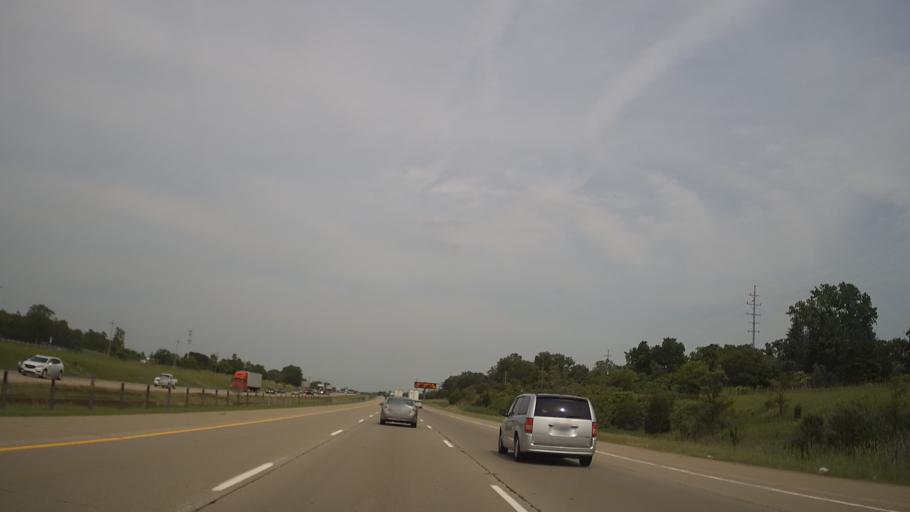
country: US
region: Michigan
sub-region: Wayne County
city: Belleville
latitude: 42.2198
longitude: -83.4759
